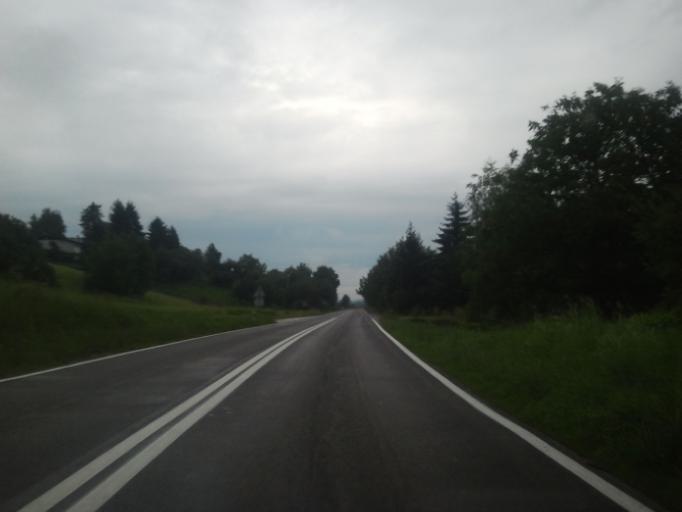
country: HR
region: Karlovacka
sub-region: Grad Karlovac
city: Karlovac
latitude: 45.4058
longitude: 15.6132
